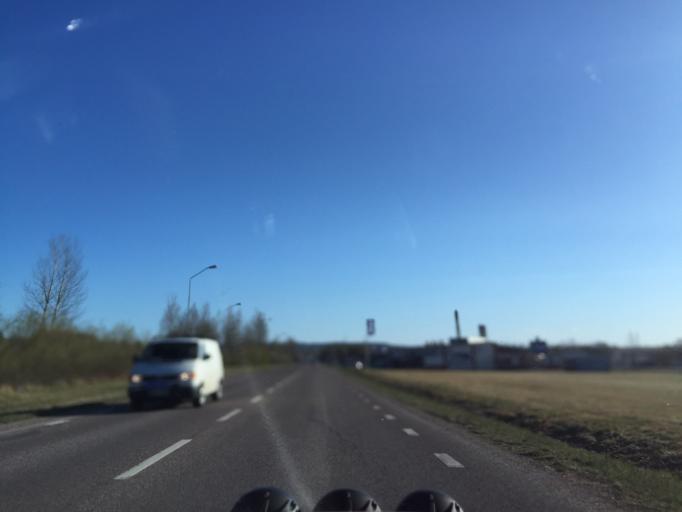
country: SE
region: Dalarna
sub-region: Borlange Kommun
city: Borlaenge
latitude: 60.4700
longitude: 15.3981
